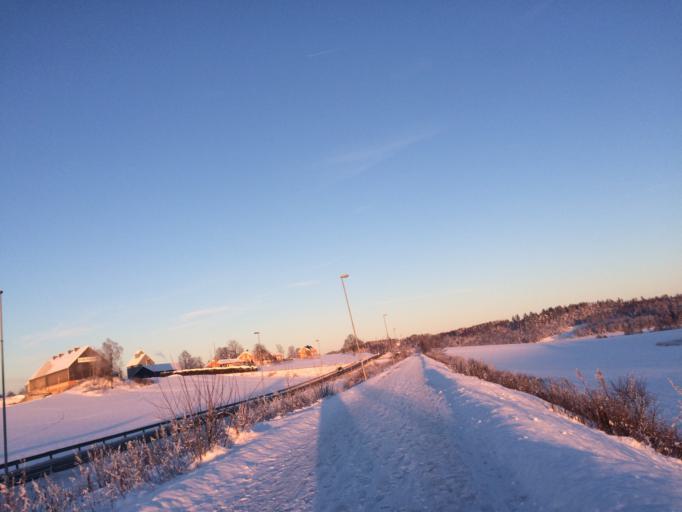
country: NO
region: Akershus
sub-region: Ski
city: Ski
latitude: 59.6926
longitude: 10.8245
